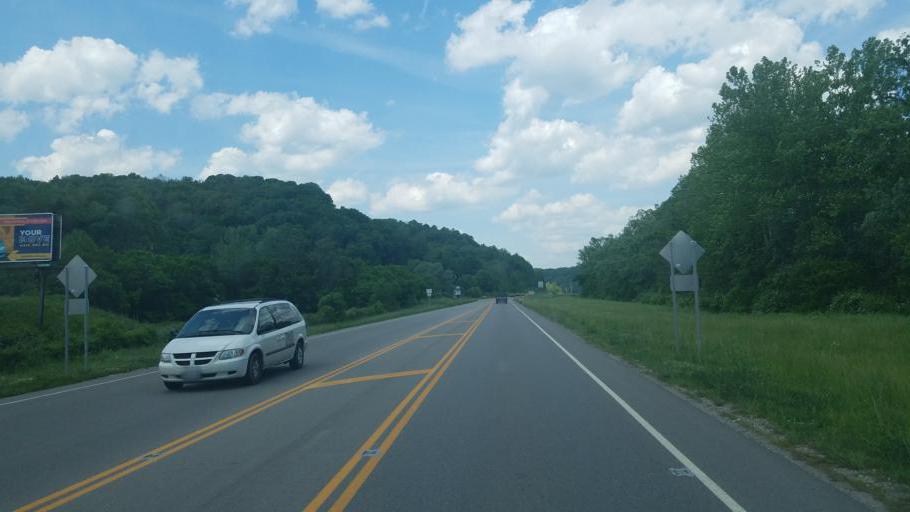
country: US
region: Ohio
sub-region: Meigs County
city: Middleport
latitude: 39.0259
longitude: -82.0661
